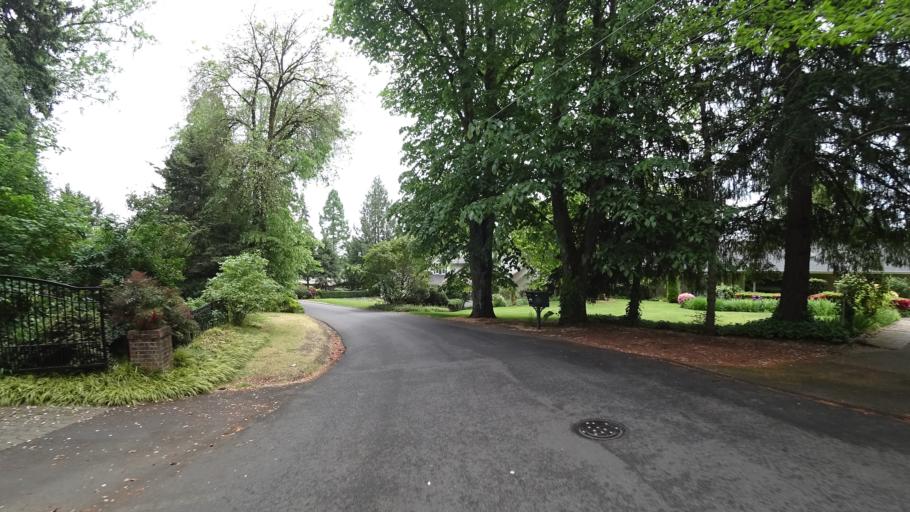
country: US
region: Oregon
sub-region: Washington County
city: Raleigh Hills
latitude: 45.4746
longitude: -122.7708
